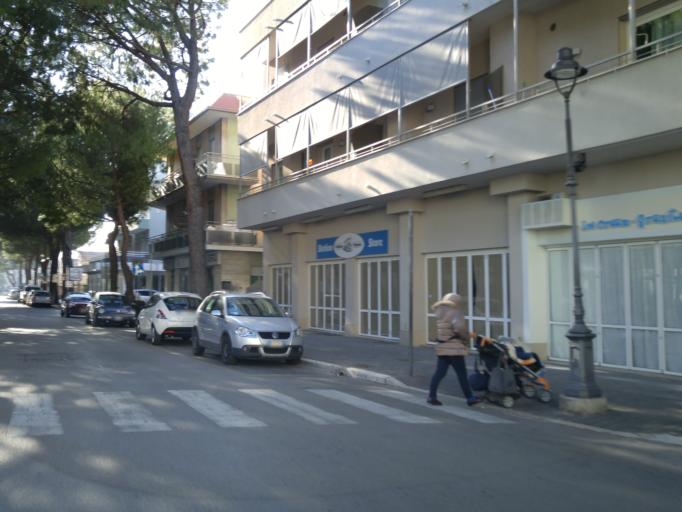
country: IT
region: The Marches
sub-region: Provincia di Pesaro e Urbino
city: Gabicce Mare
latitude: 43.9668
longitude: 12.7562
